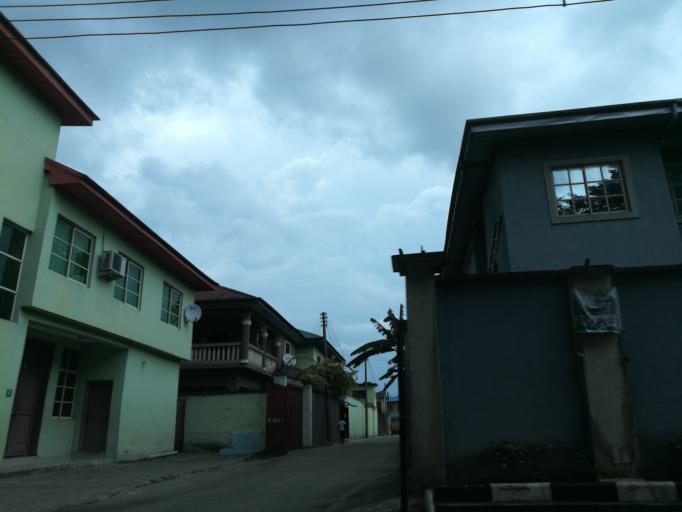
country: NG
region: Rivers
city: Port Harcourt
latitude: 4.8216
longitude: 7.0669
